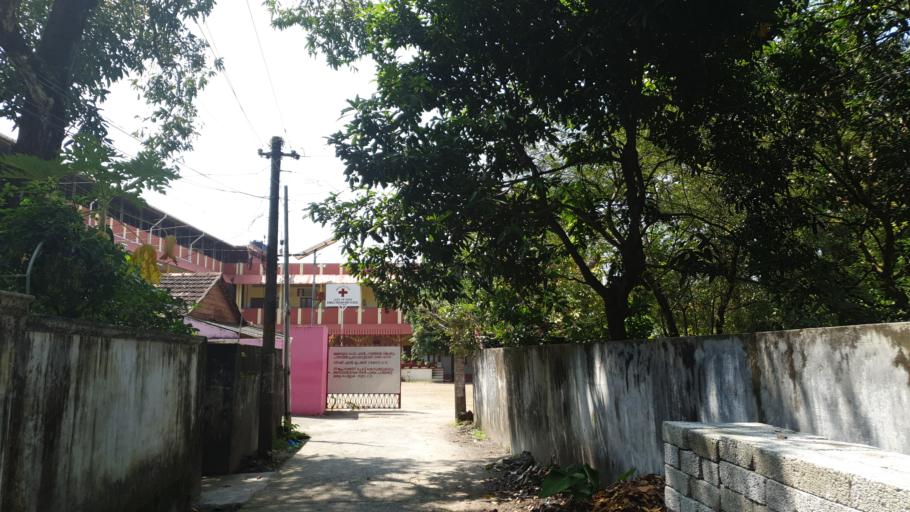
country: IN
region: Kerala
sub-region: Ernakulam
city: Cochin
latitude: 9.9752
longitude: 76.2417
